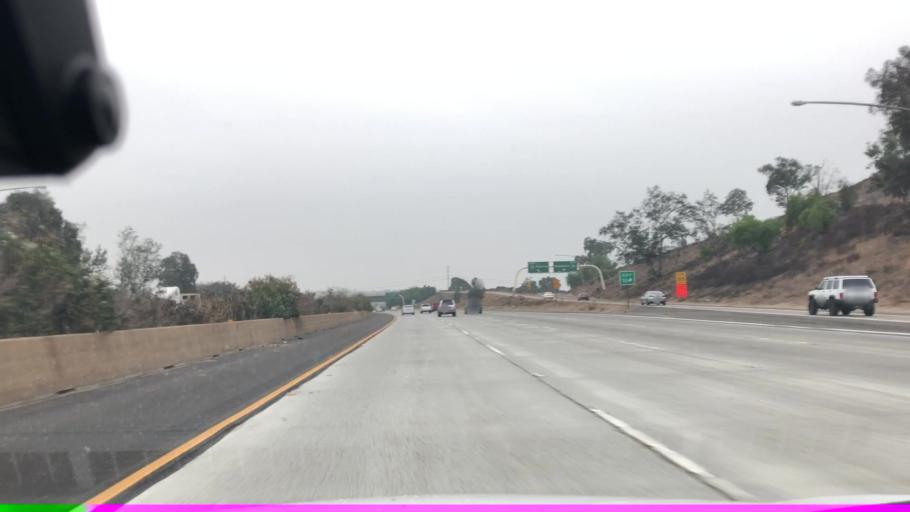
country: US
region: California
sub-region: San Diego County
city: Escondido
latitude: 33.1323
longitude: -117.1054
